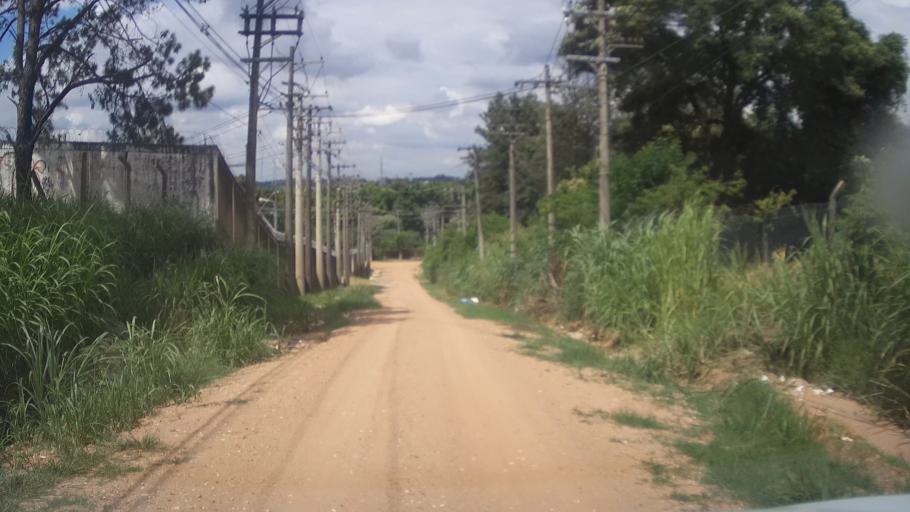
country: BR
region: Sao Paulo
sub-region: Itupeva
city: Itupeva
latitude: -23.1817
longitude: -46.9776
